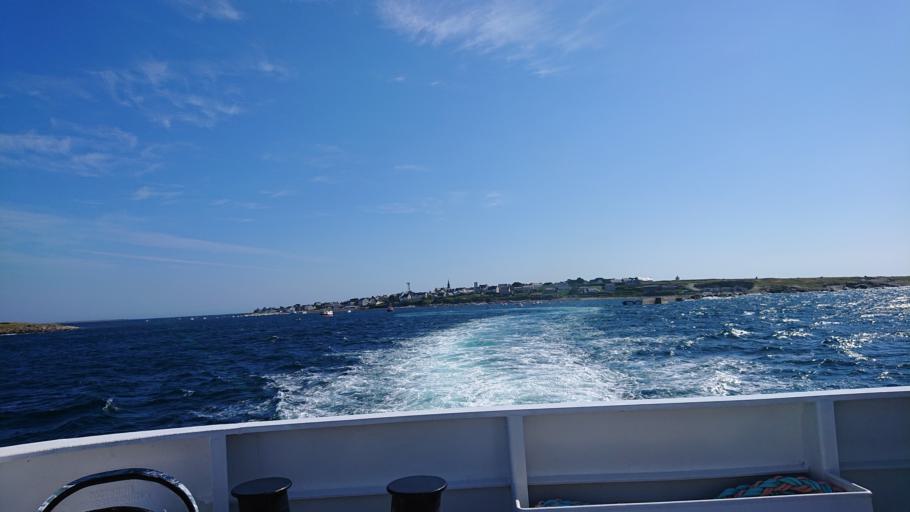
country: FR
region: Brittany
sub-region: Departement du Finistere
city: Le Conquet
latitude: 48.4046
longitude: -4.9542
